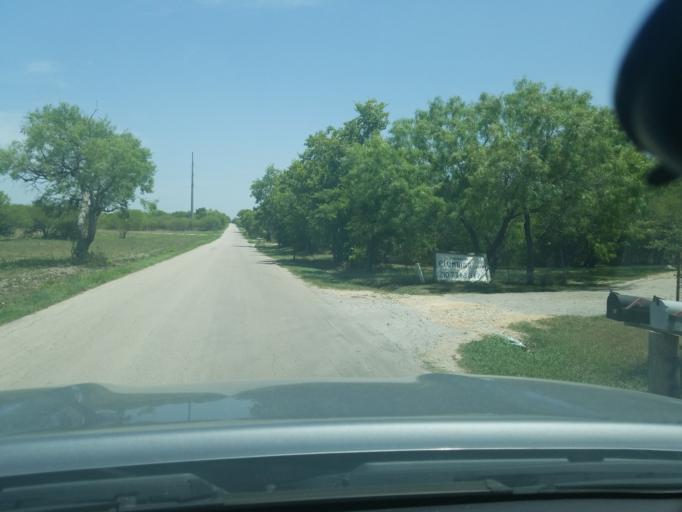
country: US
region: Texas
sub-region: Guadalupe County
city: Cibolo
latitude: 29.5841
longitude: -98.2008
